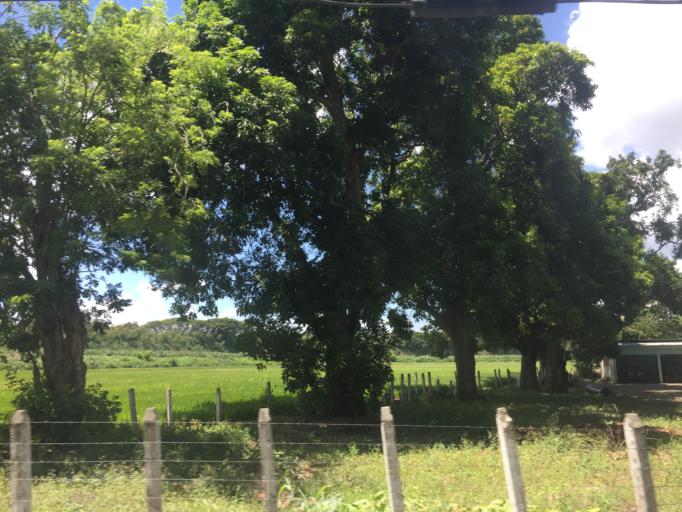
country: DO
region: Santiago
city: Santiago de los Caballeros
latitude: 19.4519
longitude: -70.7507
